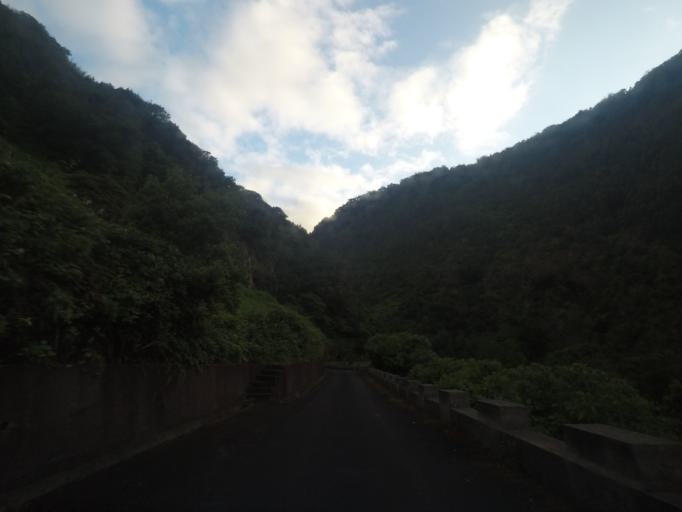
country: PT
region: Madeira
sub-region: Porto Moniz
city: Porto Moniz
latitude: 32.8475
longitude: -17.1622
